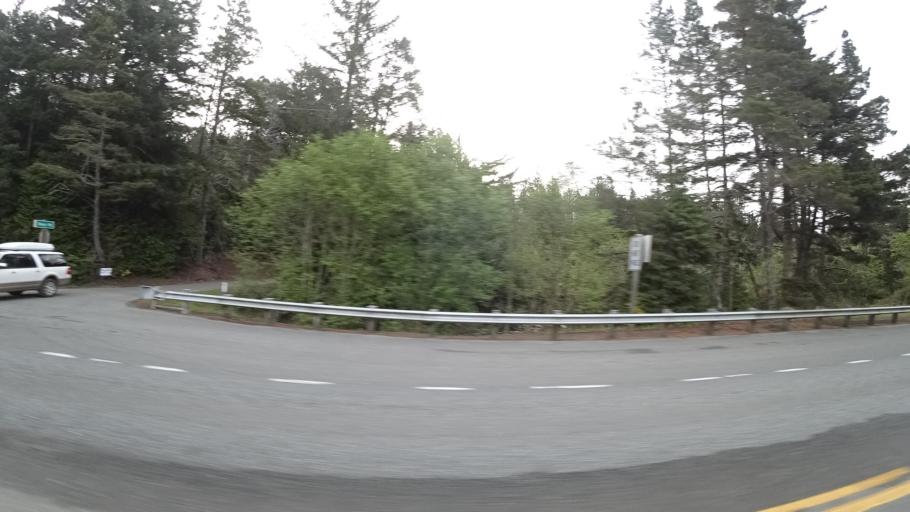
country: US
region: Oregon
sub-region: Coos County
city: Lakeside
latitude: 43.5280
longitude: -124.2160
